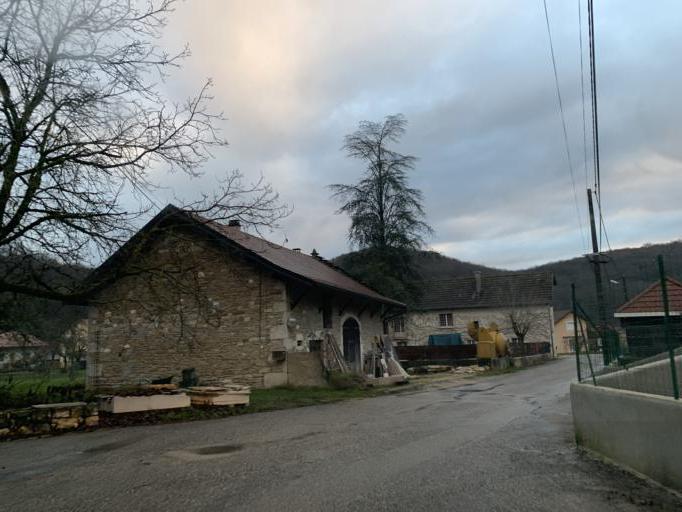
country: FR
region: Rhone-Alpes
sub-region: Departement de l'Ain
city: Belley
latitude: 45.7995
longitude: 5.6915
